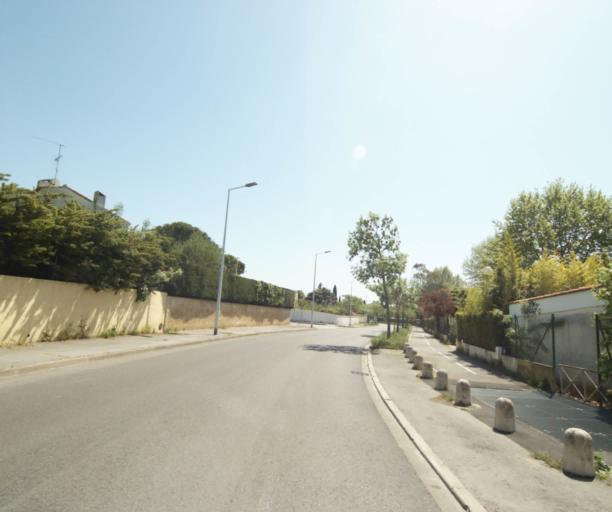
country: FR
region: Languedoc-Roussillon
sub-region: Departement de l'Herault
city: Saint-Jean-de-Vedas
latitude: 43.6013
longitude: 3.8344
